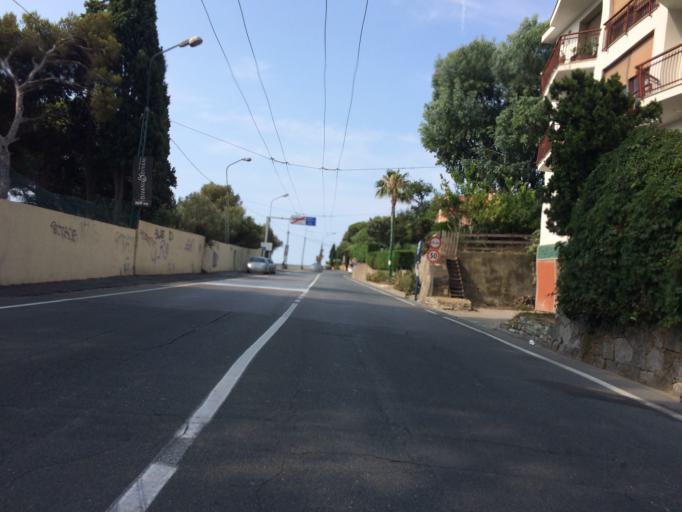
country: IT
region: Liguria
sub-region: Provincia di Imperia
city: Ospedaletti
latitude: 43.8022
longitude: 7.7443
